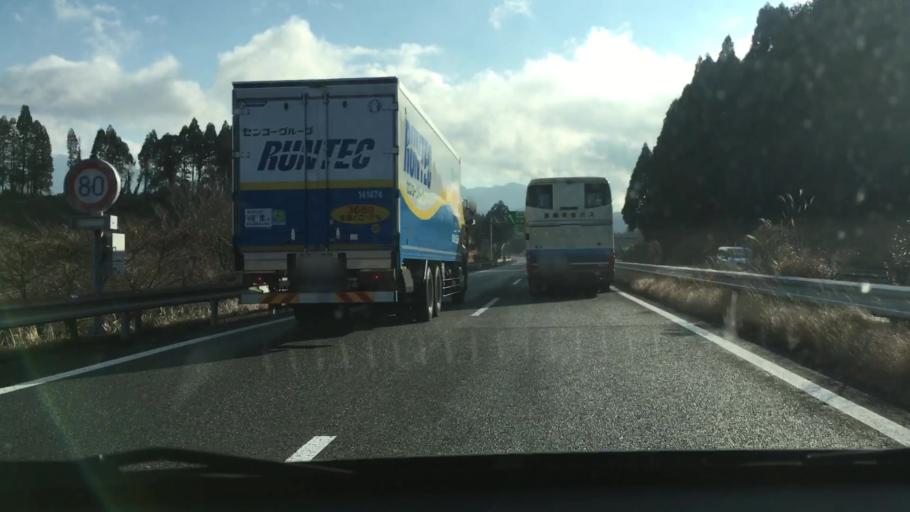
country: JP
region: Kagoshima
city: Okuchi-shinohara
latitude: 32.0384
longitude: 130.7992
